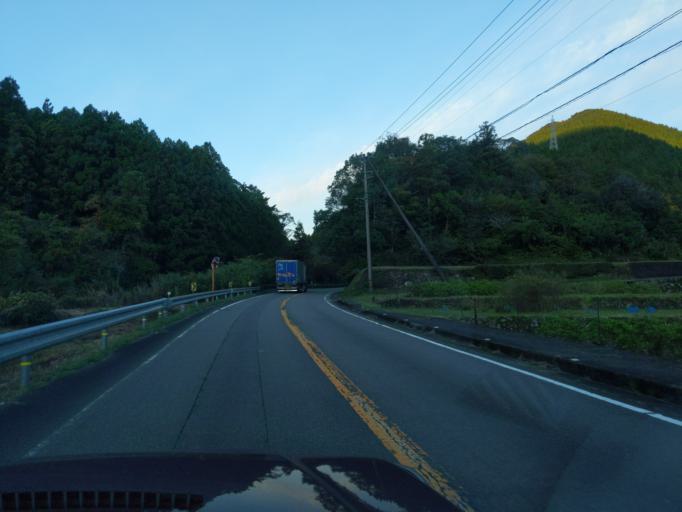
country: JP
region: Tokushima
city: Anan
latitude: 33.7074
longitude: 134.4627
